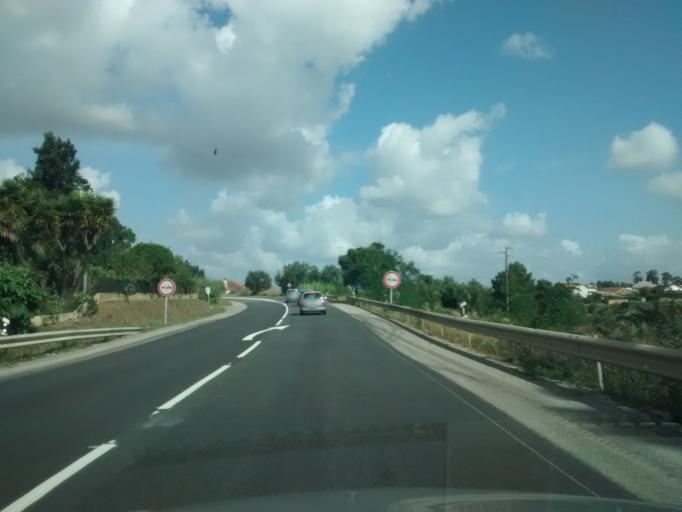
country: PT
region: Aveiro
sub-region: Oliveira do Bairro
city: Oia
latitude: 40.5458
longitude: -8.5354
